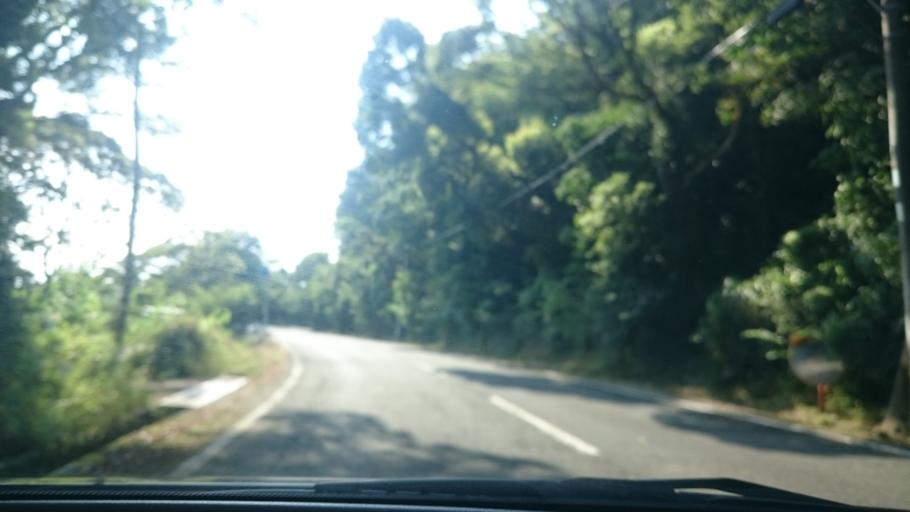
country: JP
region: Shizuoka
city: Heda
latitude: 34.9805
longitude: 138.7783
